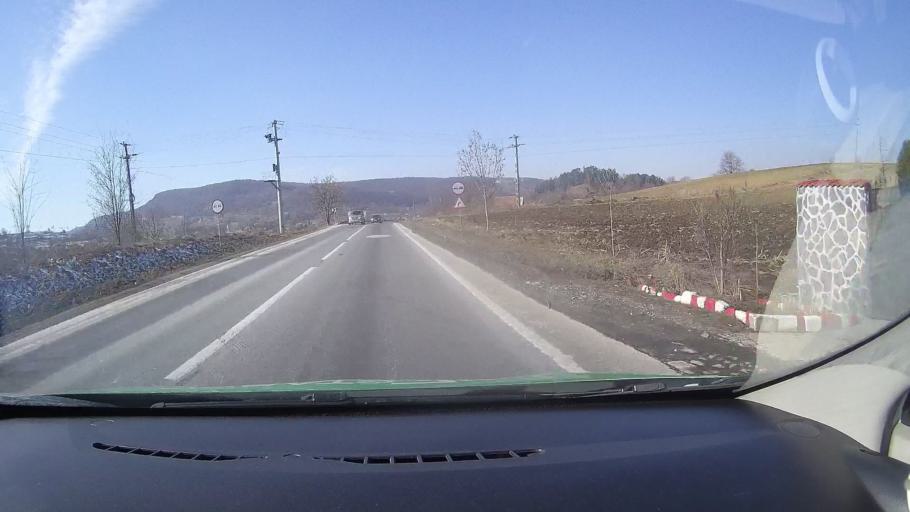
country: RO
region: Mures
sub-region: Comuna Saschiz
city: Saschiz
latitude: 46.1844
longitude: 24.9695
